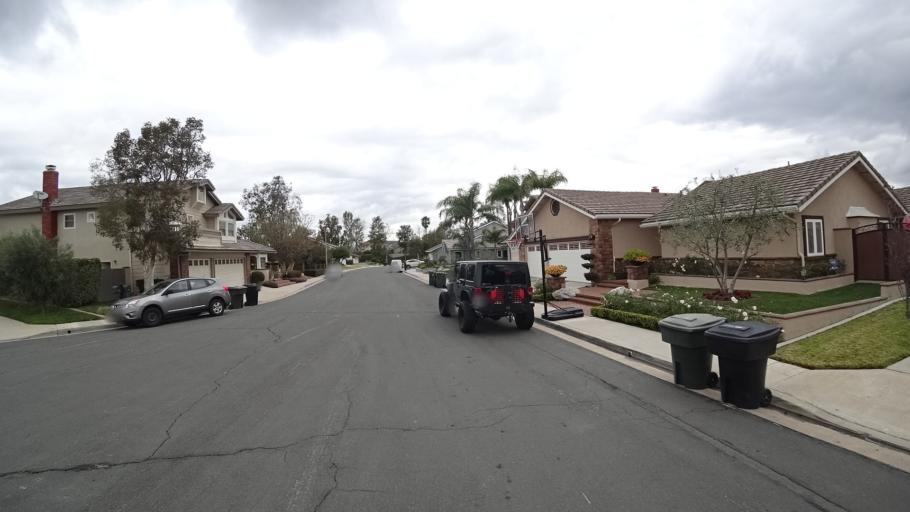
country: US
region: California
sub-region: Orange County
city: Villa Park
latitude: 33.8420
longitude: -117.7527
